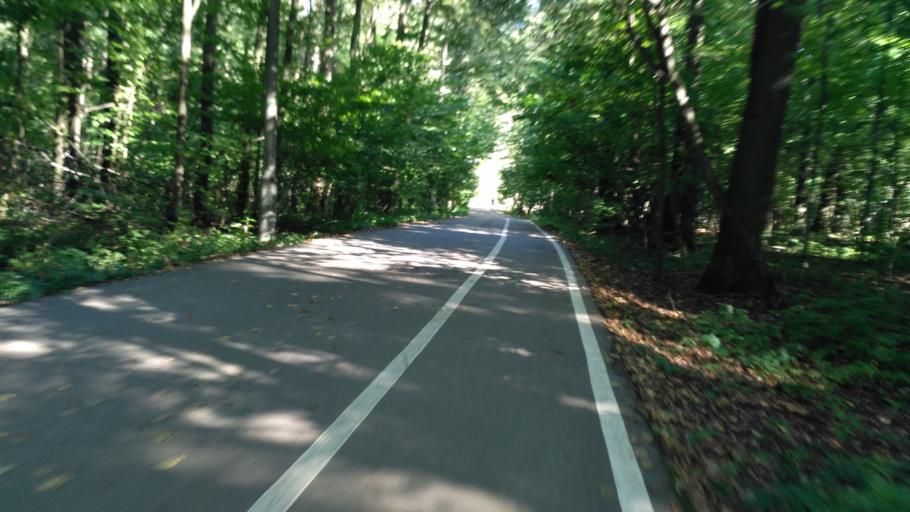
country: RU
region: Moskovskaya
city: Izmaylovo
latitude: 55.7756
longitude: 37.7722
